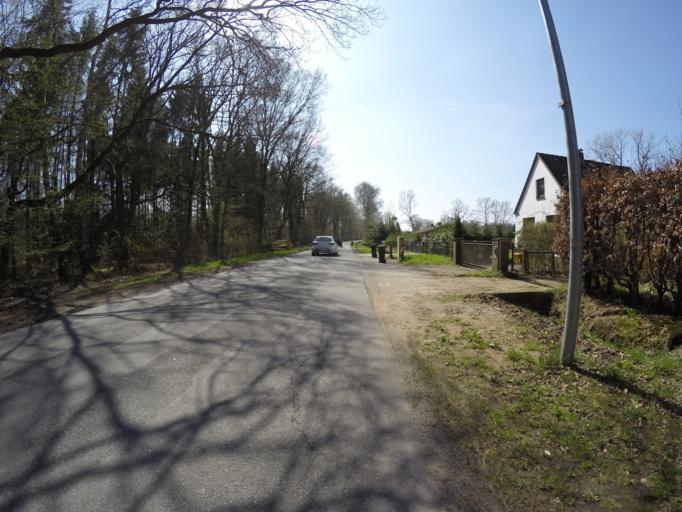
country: DE
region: Schleswig-Holstein
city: Quickborn
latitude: 53.7195
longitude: 9.9231
